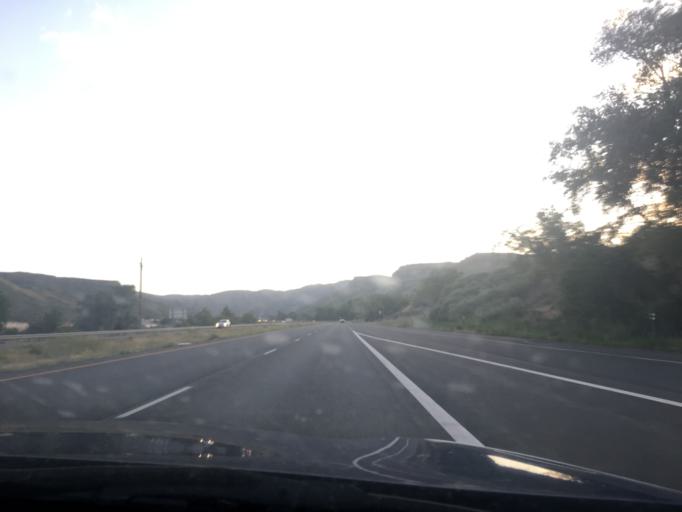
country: US
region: Colorado
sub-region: Jefferson County
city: Applewood
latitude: 39.7725
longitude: -105.1794
